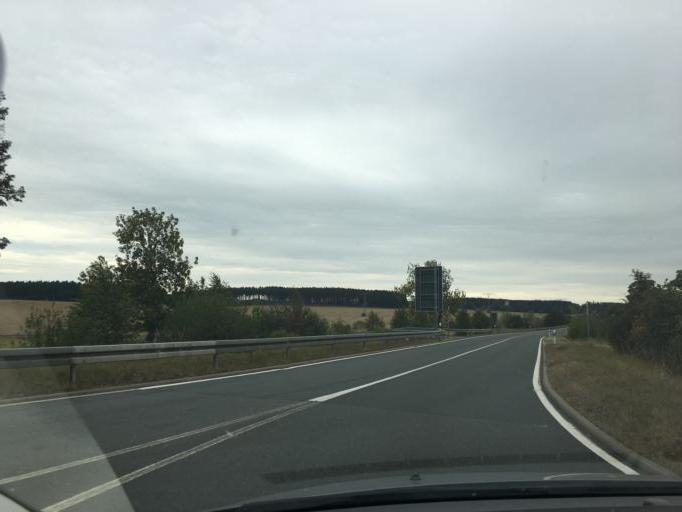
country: DE
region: Thuringia
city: Bad Lobenstein
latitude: 50.4791
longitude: 11.6367
